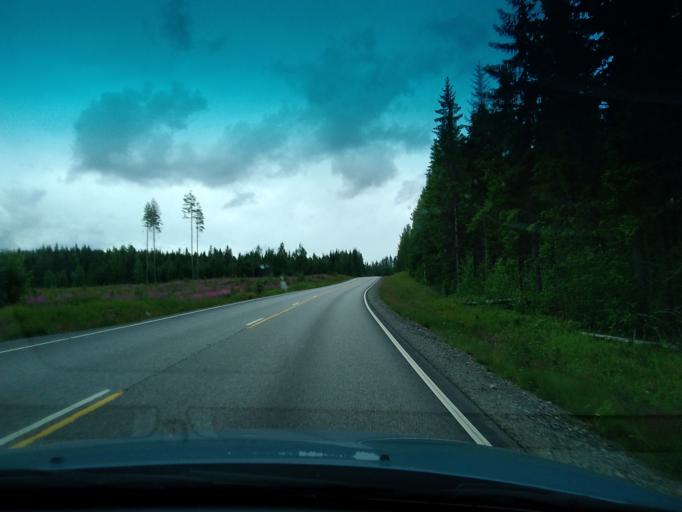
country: FI
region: Central Finland
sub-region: Keuruu
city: Multia
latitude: 62.4582
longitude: 24.7204
